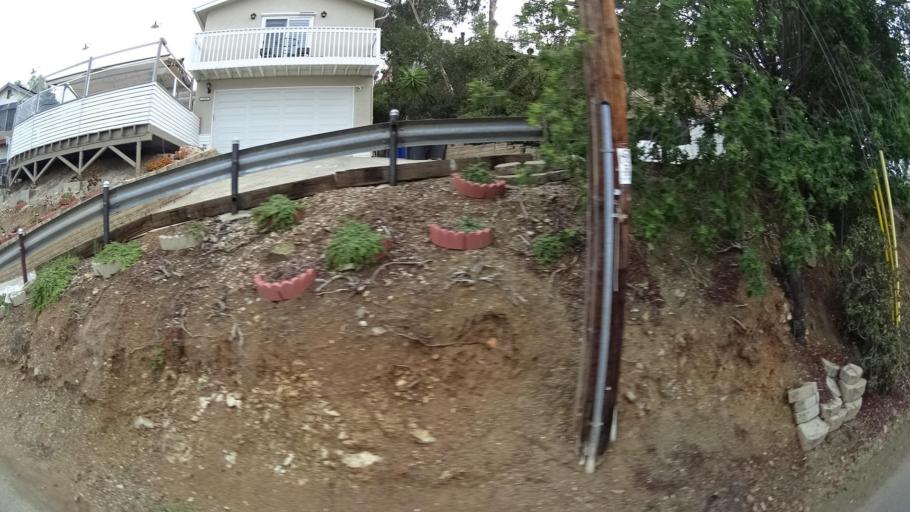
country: US
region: California
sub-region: San Diego County
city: Spring Valley
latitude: 32.7433
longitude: -117.0120
